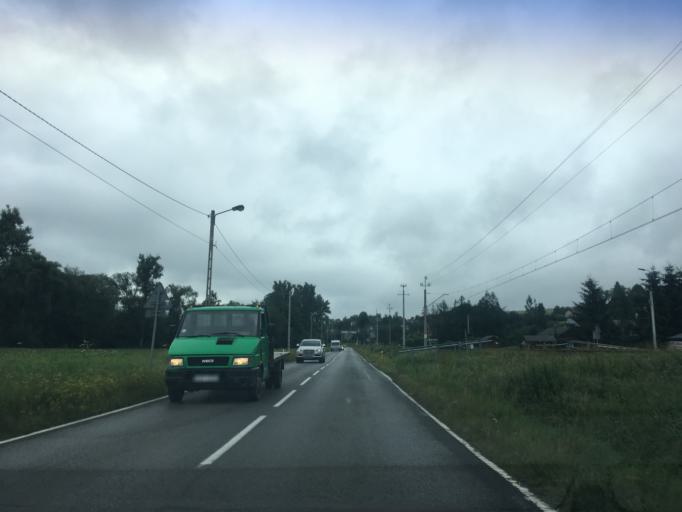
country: PL
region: Lesser Poland Voivodeship
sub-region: Powiat nowotarski
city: Rokiciny
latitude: 49.5812
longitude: 19.9109
